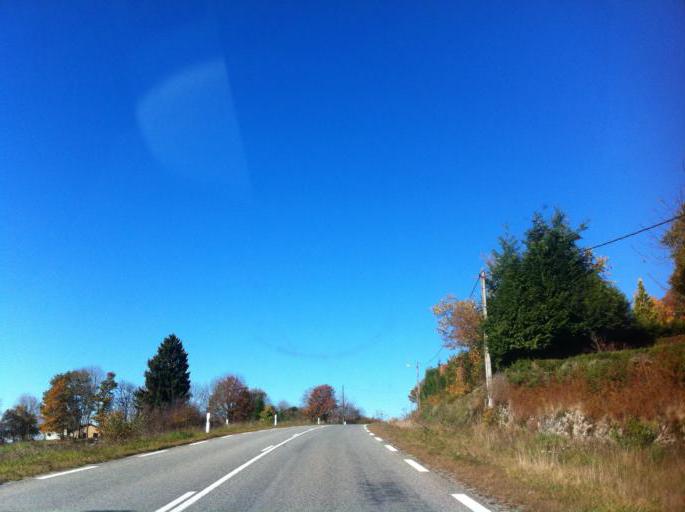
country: FR
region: Auvergne
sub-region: Departement du Puy-de-Dome
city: Gelles
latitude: 45.8597
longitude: 2.6132
